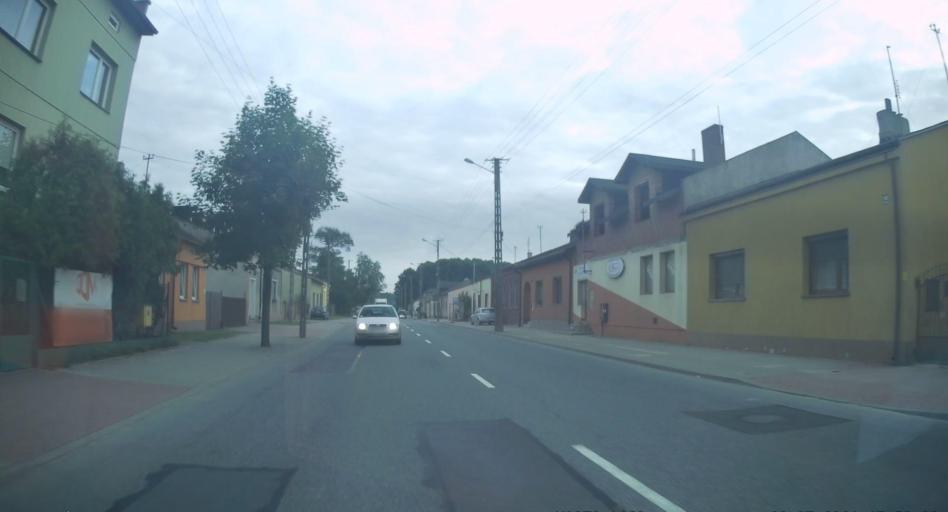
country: PL
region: Lodz Voivodeship
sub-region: Powiat radomszczanski
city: Kamiensk
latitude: 51.1922
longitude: 19.4982
